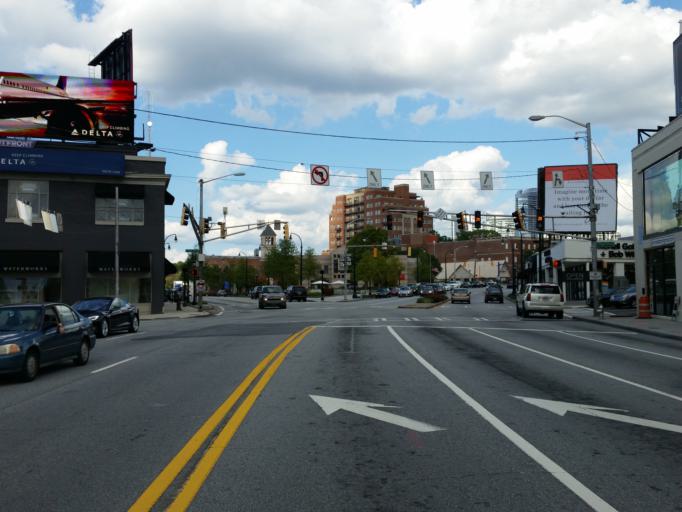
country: US
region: Georgia
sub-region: DeKalb County
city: North Atlanta
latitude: 33.8391
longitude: -84.3802
